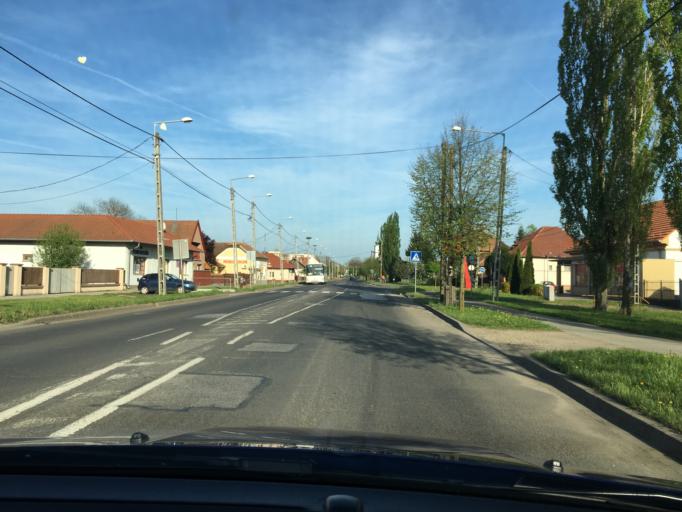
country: HU
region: Bekes
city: Szeghalom
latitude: 47.0161
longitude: 21.1667
